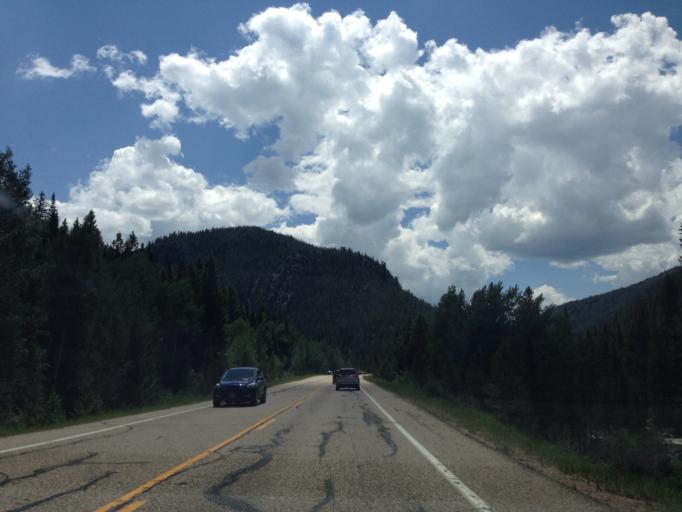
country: US
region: Colorado
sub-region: Larimer County
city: Estes Park
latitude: 40.6369
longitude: -105.8056
